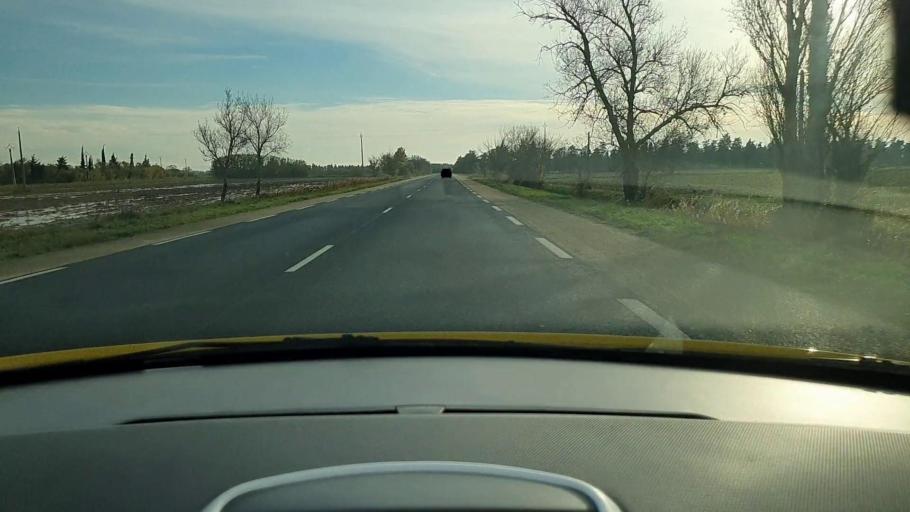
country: FR
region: Languedoc-Roussillon
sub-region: Departement du Gard
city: Fourques
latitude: 43.7059
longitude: 4.5610
